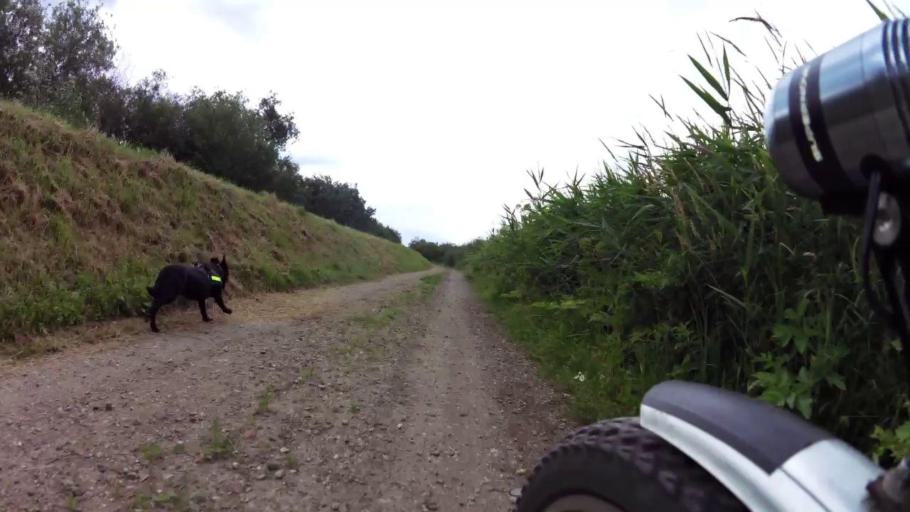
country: PL
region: West Pomeranian Voivodeship
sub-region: Powiat policki
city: Police
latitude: 53.5997
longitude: 14.5654
